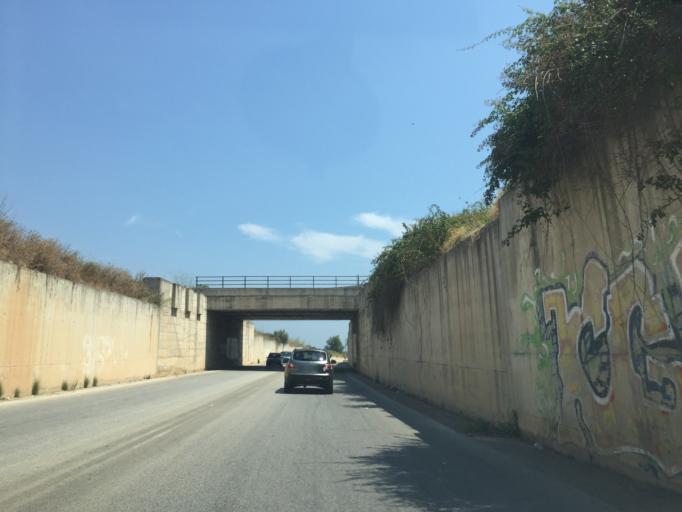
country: IT
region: Sicily
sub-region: Provincia di Siracusa
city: Avola
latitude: 36.9208
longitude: 15.1373
